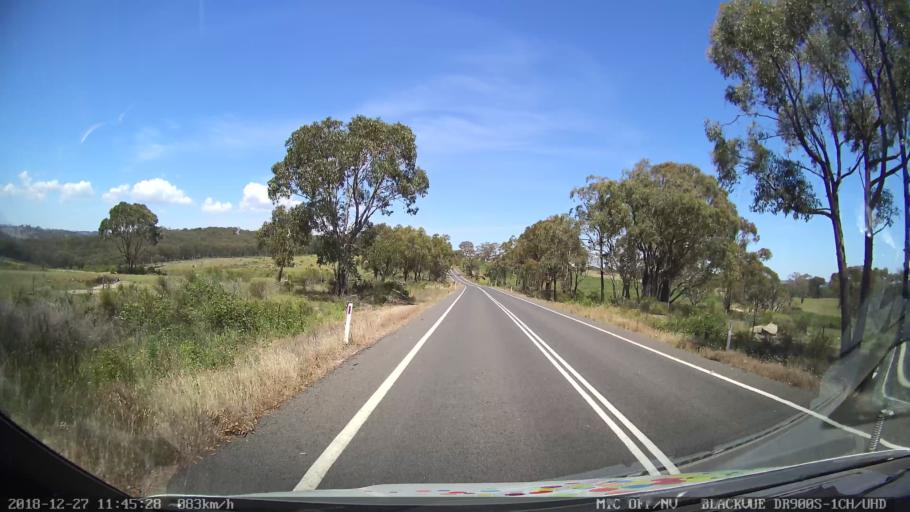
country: AU
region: New South Wales
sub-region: Bathurst Regional
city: Perthville
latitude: -33.5821
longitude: 149.4694
